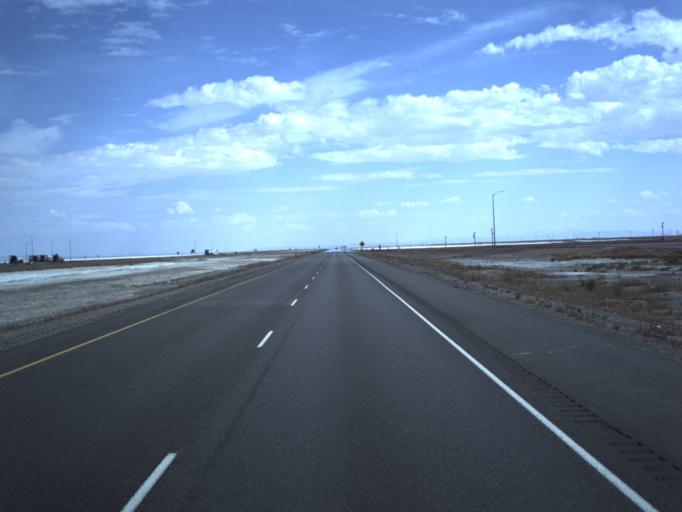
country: US
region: Utah
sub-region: Tooele County
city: Wendover
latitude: 40.7386
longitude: -113.8583
